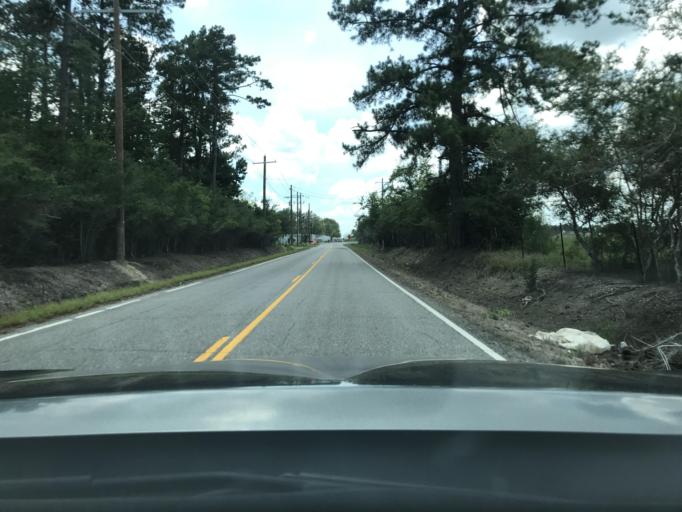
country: US
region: Louisiana
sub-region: Calcasieu Parish
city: Moss Bluff
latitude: 30.3300
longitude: -93.1664
